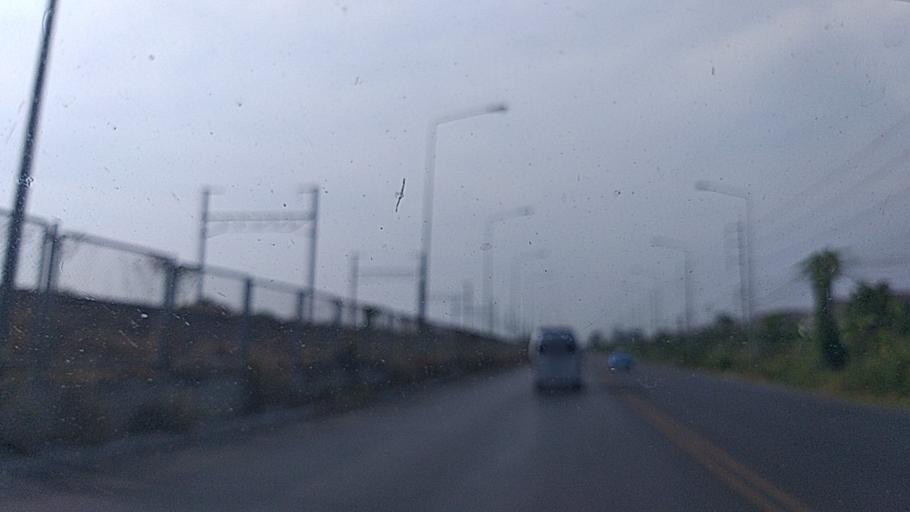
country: TH
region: Phra Nakhon Si Ayutthaya
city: Ban Bang Kadi Pathum Thani
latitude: 13.9797
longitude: 100.6034
